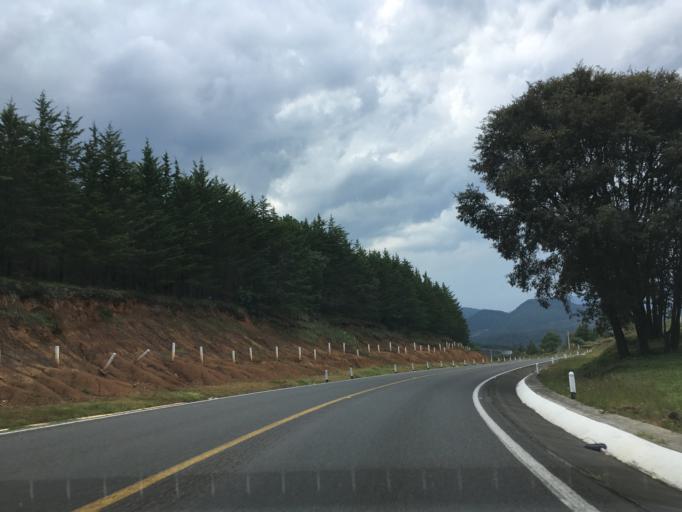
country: MX
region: Michoacan
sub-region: Patzcuaro
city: Santa Ana Chapitiro
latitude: 19.5065
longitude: -101.6933
